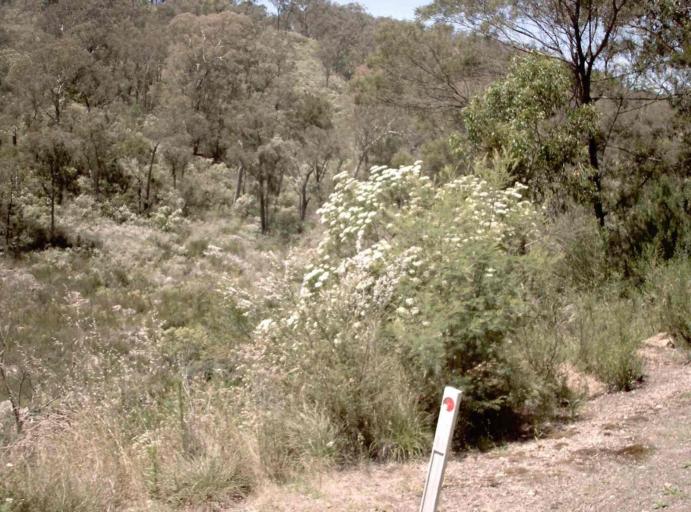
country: AU
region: Victoria
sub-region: East Gippsland
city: Bairnsdale
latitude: -37.4859
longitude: 147.8328
